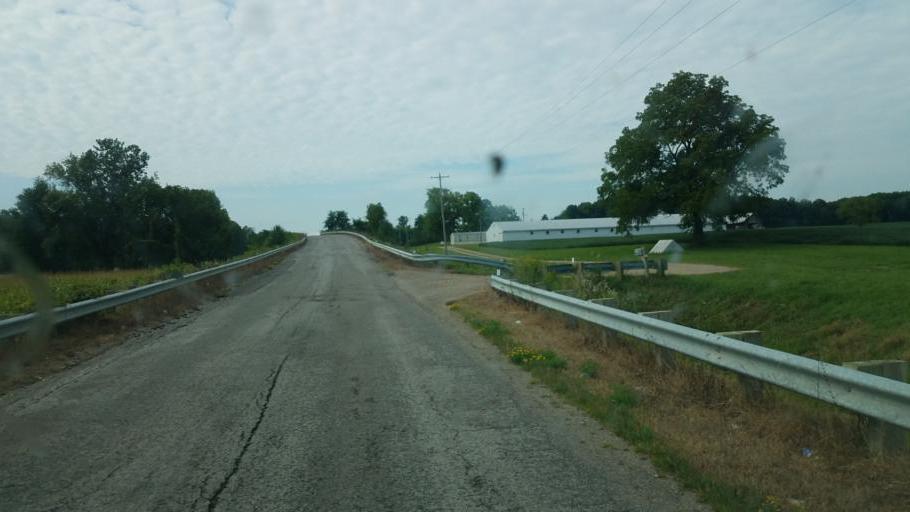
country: US
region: Ohio
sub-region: Morrow County
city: Mount Gilead
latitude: 40.4712
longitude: -82.7586
